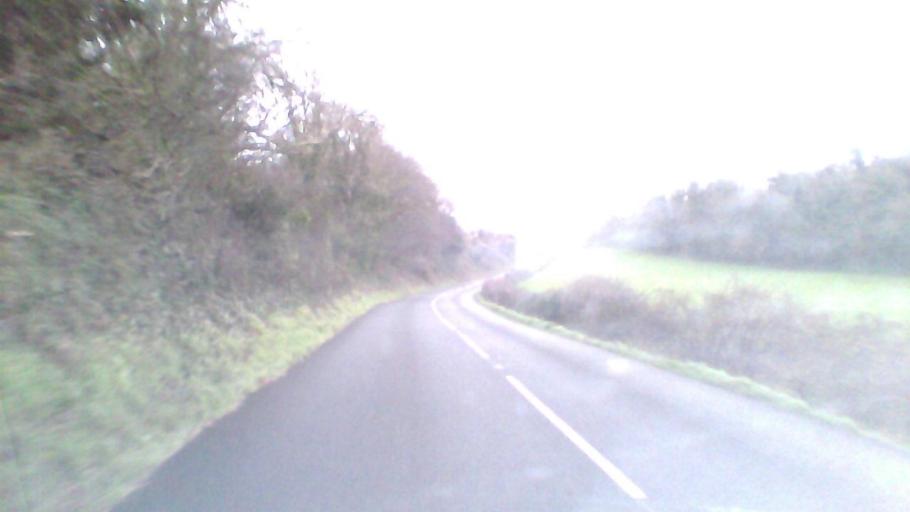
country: GB
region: England
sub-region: Isle of Wight
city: Brading
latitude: 50.6730
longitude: -1.1388
